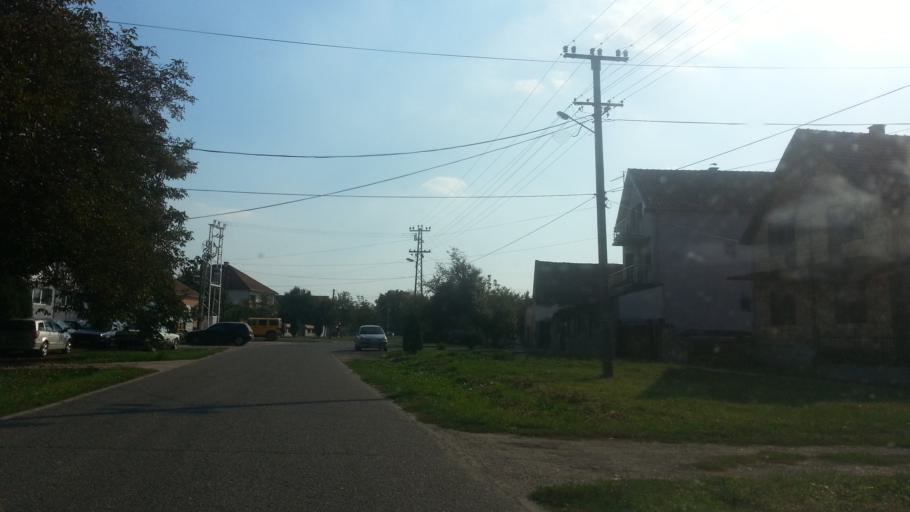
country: RS
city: Stari Banovci
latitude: 44.9863
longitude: 20.2743
